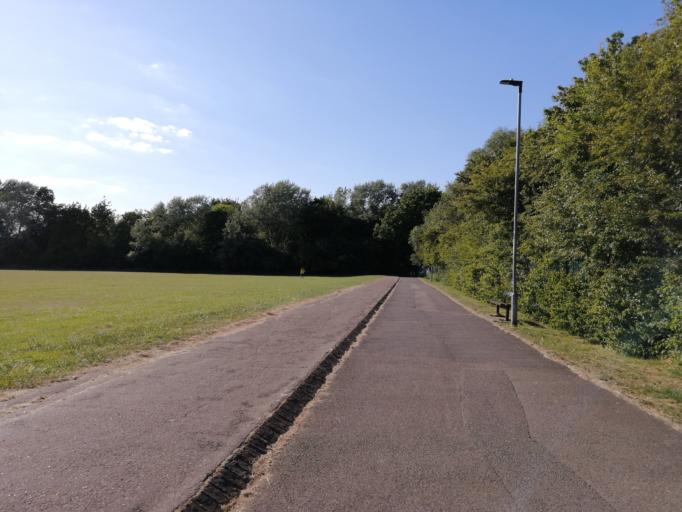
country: GB
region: England
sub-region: Peterborough
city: Marholm
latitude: 52.5960
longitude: -0.2754
